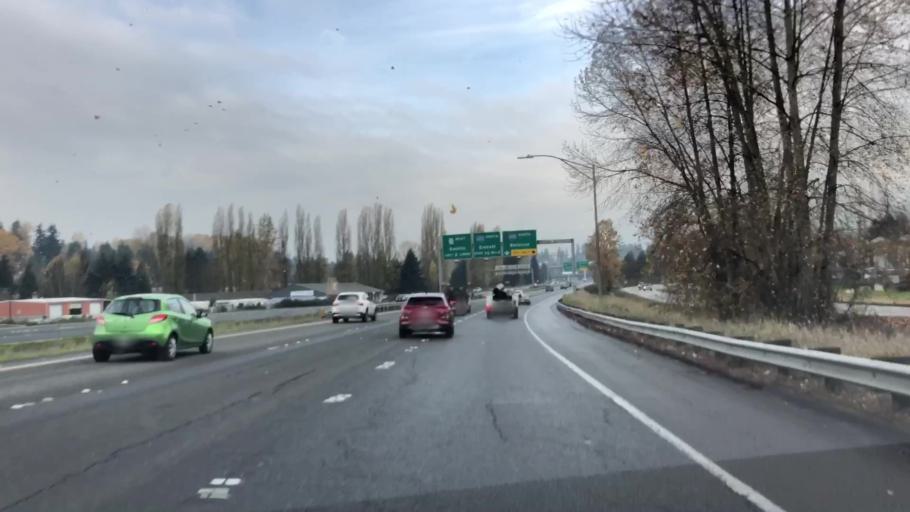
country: US
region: Washington
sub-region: King County
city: Woodinville
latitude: 47.7576
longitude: -122.1688
